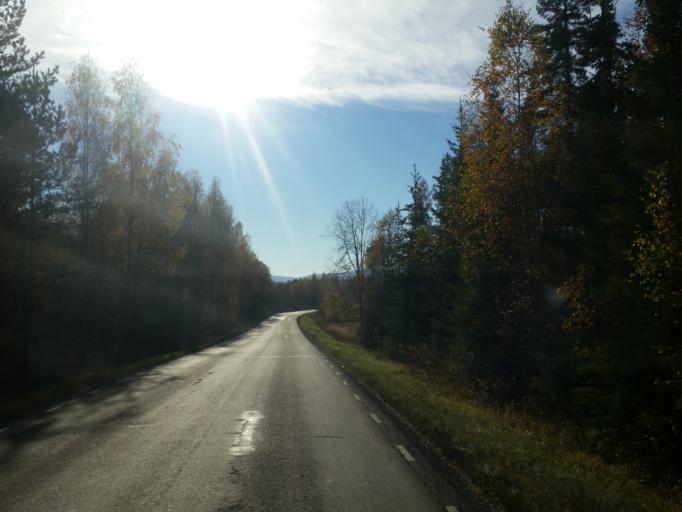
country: SE
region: Dalarna
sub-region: Borlange Kommun
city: Ornas
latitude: 60.5094
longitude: 15.5223
